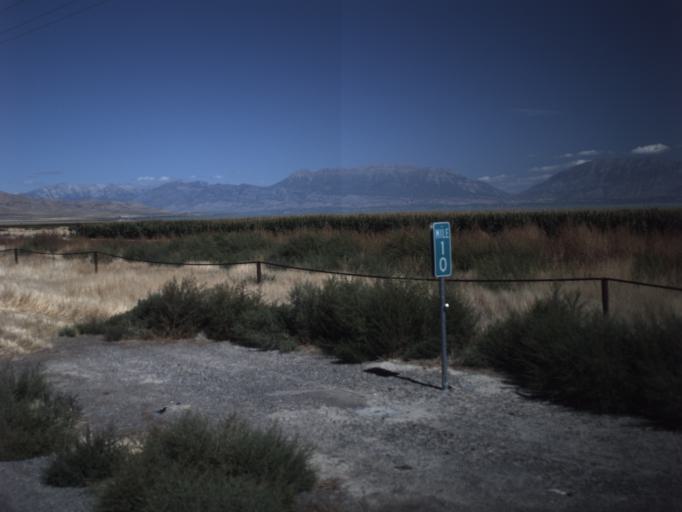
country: US
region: Utah
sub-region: Utah County
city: Genola
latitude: 40.0971
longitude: -111.9590
